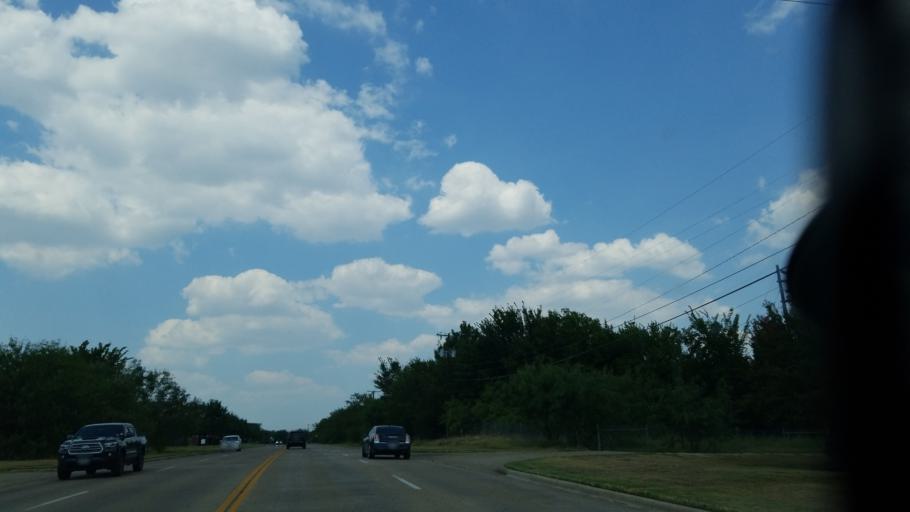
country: US
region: Texas
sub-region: Dallas County
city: Grand Prairie
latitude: 32.7315
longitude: -96.9858
